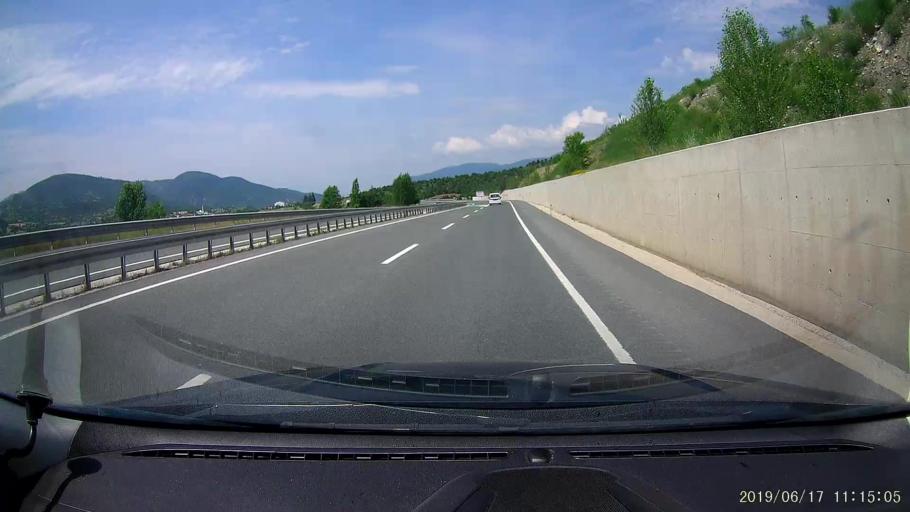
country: TR
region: Kastamonu
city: Tosya
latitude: 40.9539
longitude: 33.9306
